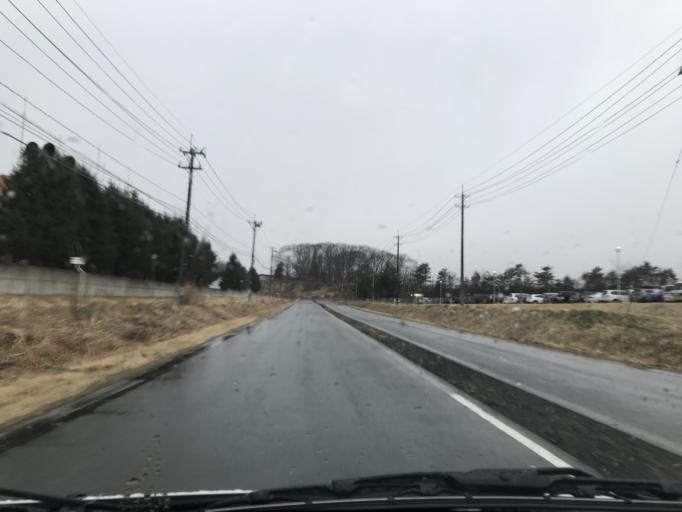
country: JP
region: Iwate
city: Kitakami
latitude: 39.2142
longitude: 141.0662
